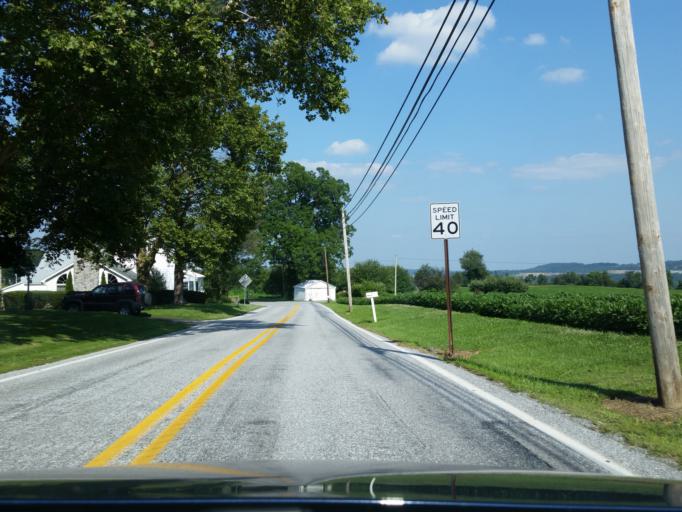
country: US
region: Pennsylvania
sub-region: Lancaster County
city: Marietta
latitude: 40.0314
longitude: -76.5744
